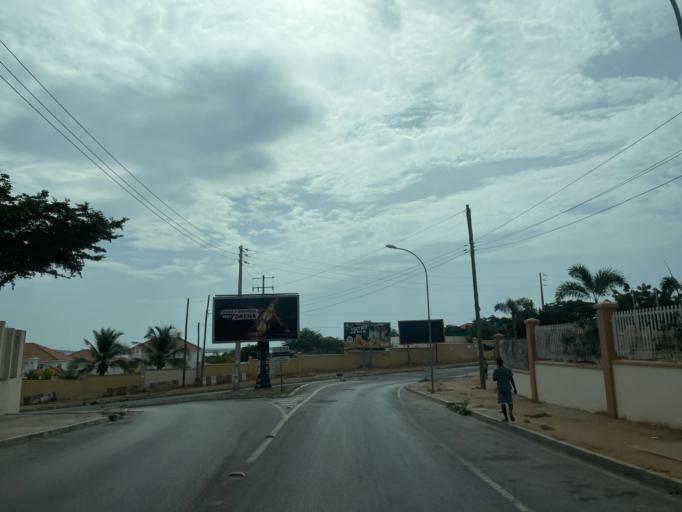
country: AO
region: Luanda
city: Luanda
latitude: -8.9218
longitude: 13.1708
